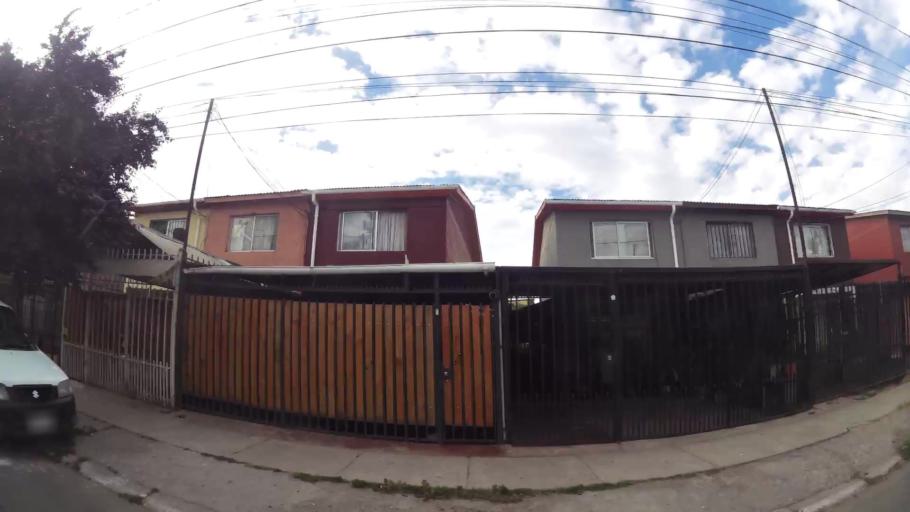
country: CL
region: Santiago Metropolitan
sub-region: Provincia de Cordillera
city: Puente Alto
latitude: -33.6235
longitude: -70.6113
